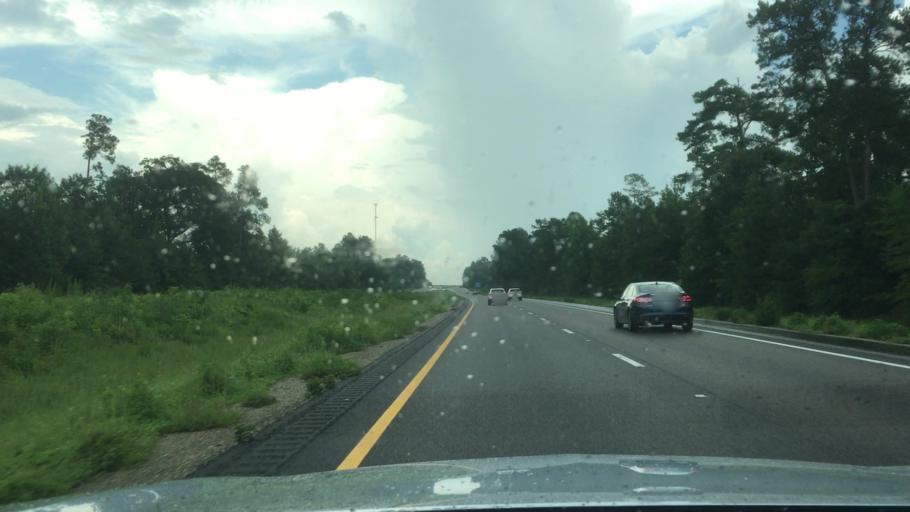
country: US
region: Mississippi
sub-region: Lamar County
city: Purvis
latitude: 31.1786
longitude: -89.3467
